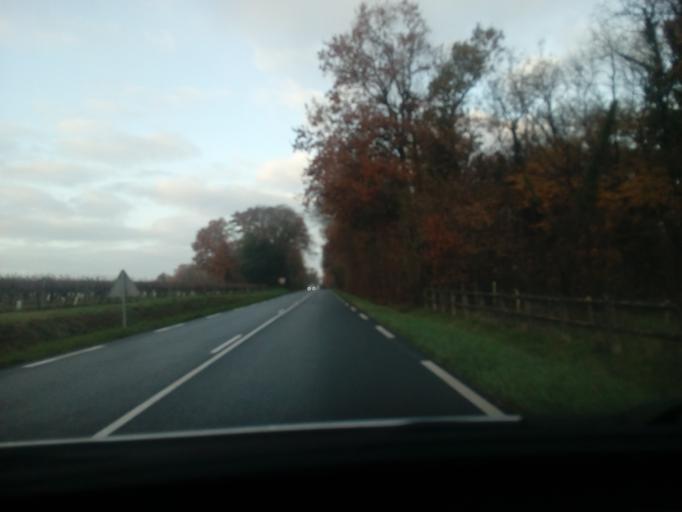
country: FR
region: Poitou-Charentes
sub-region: Departement de la Charente-Maritime
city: Jonzac
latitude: 45.4429
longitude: -0.3601
